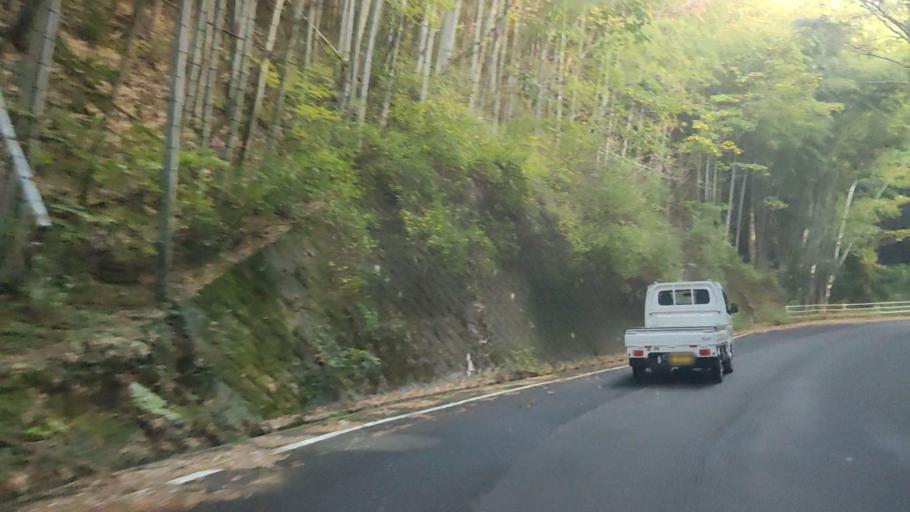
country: JP
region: Shizuoka
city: Mishima
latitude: 35.1320
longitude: 138.9853
